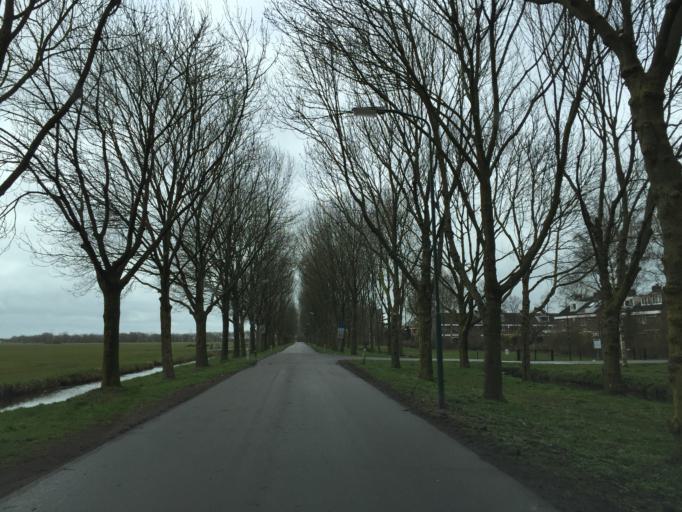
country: NL
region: Utrecht
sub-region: Gemeente Montfoort
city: Montfoort
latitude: 52.0844
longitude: 4.9578
